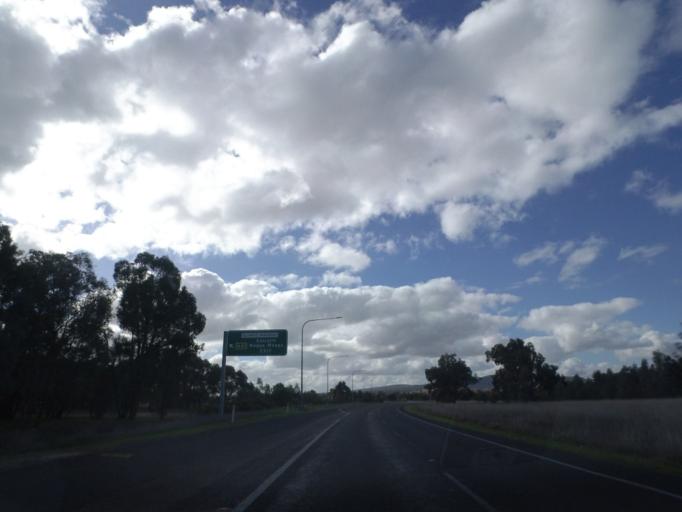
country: AU
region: New South Wales
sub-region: Greater Hume Shire
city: Jindera
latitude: -35.9298
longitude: 147.0032
